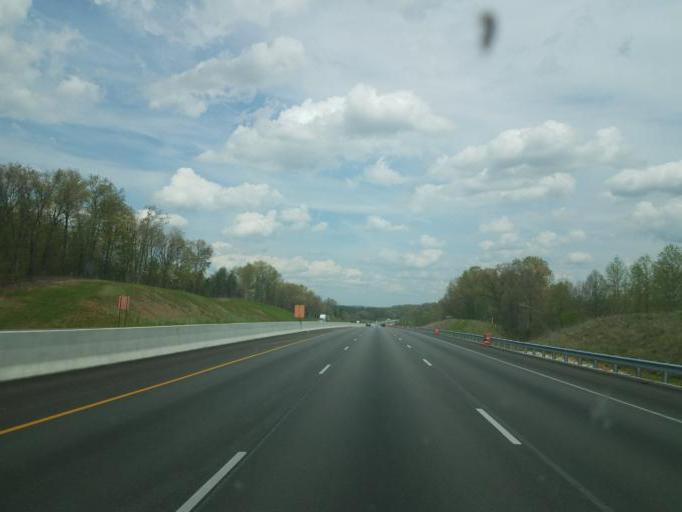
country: US
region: Kentucky
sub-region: Hart County
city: Munfordville
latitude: 37.3253
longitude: -85.9063
